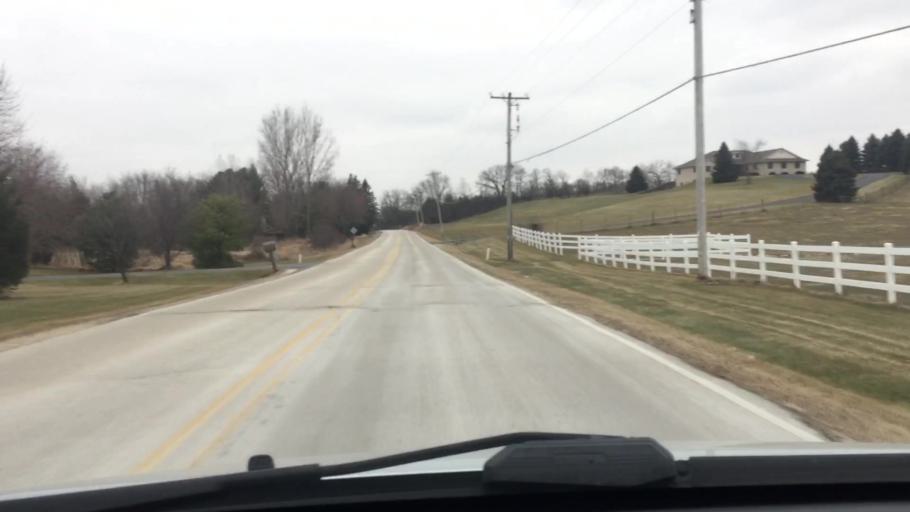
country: US
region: Wisconsin
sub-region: Waukesha County
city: Wales
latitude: 43.0196
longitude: -88.3448
